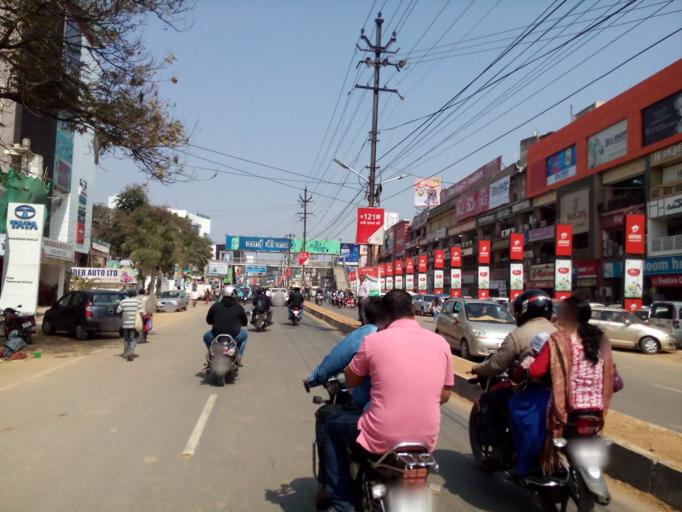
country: IN
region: Jharkhand
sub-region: Ranchi
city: Ranchi
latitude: 23.3573
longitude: 85.3247
